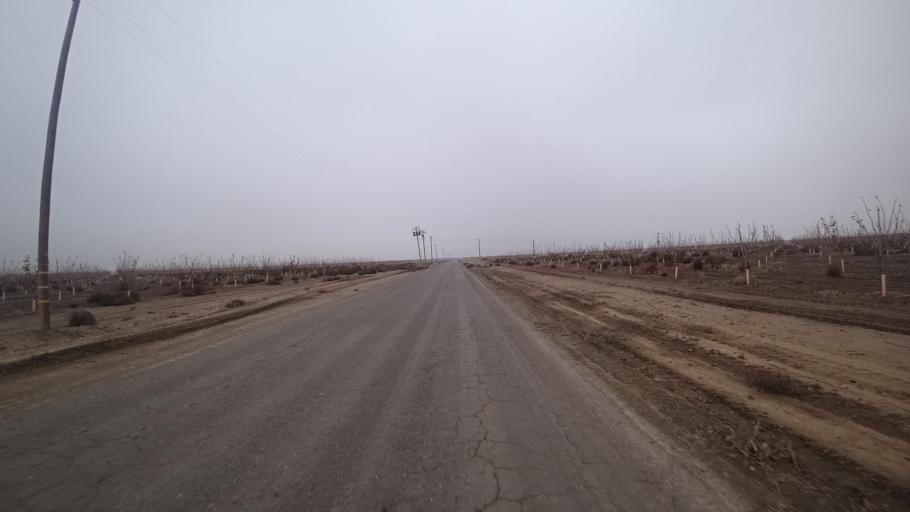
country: US
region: California
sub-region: Kern County
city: Wasco
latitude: 35.6974
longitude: -119.4195
